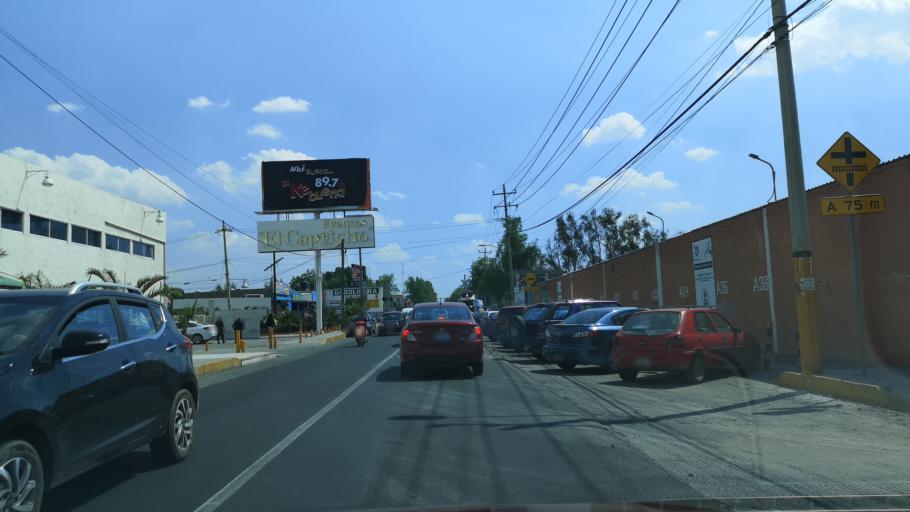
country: MX
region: Puebla
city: Puebla
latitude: 19.0812
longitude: -98.2161
